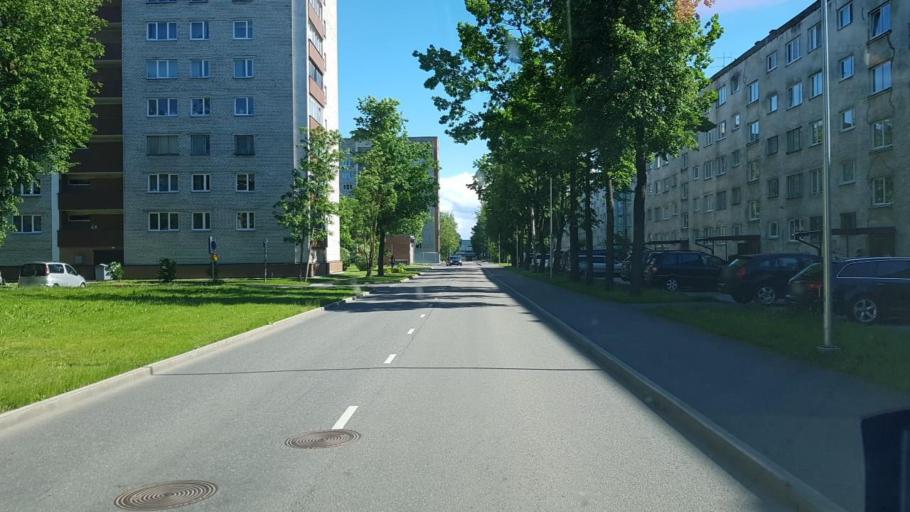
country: EE
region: Ida-Virumaa
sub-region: Narva linn
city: Narva
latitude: 59.3682
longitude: 28.1804
